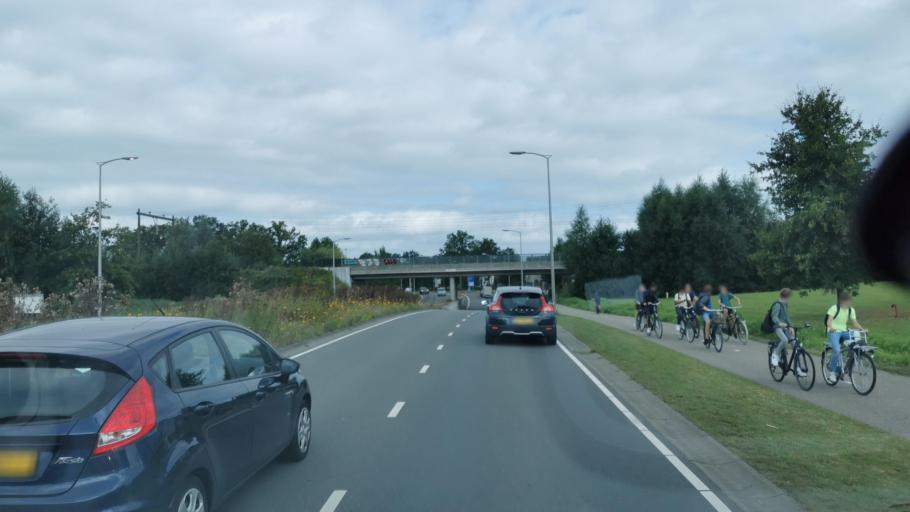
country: NL
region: Overijssel
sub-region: Gemeente Oldenzaal
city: Oldenzaal
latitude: 52.3033
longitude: 6.9223
